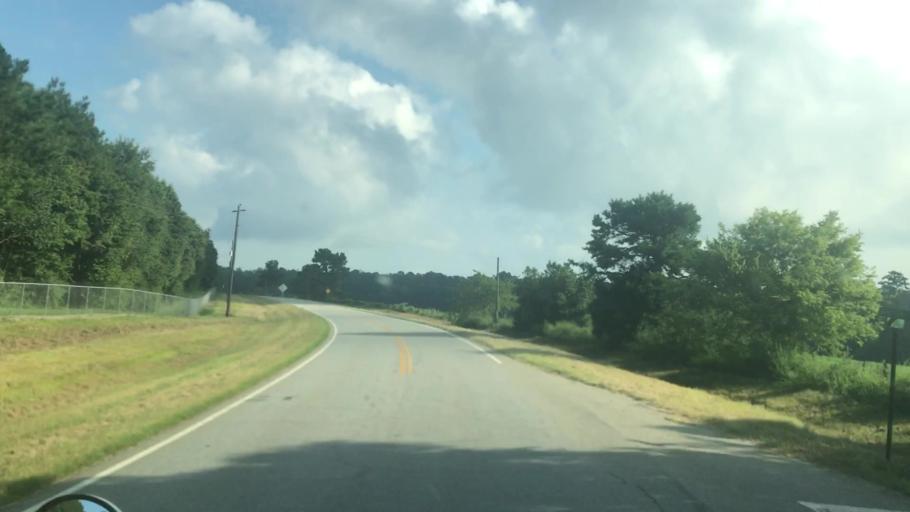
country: US
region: Florida
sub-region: Gadsden County
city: Havana
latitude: 30.7377
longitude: -84.4807
